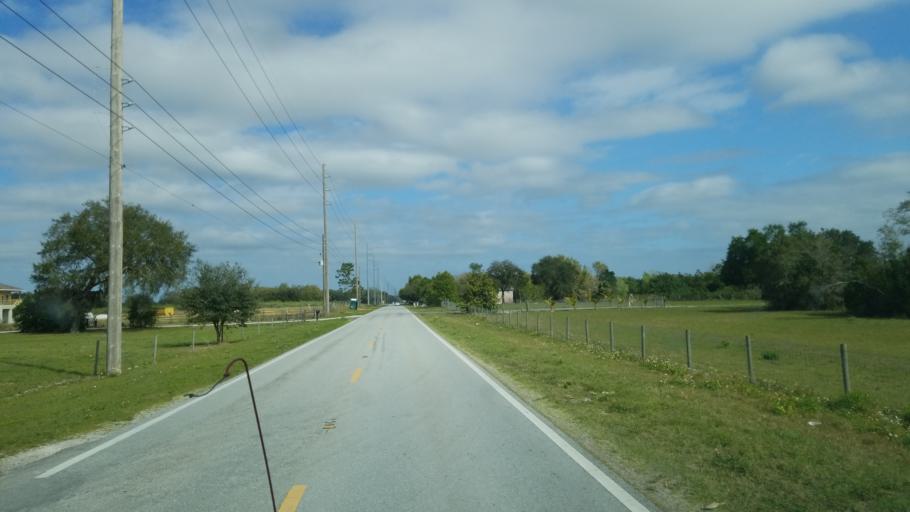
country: US
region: Florida
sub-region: Polk County
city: Lake Wales
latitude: 27.9351
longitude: -81.5376
